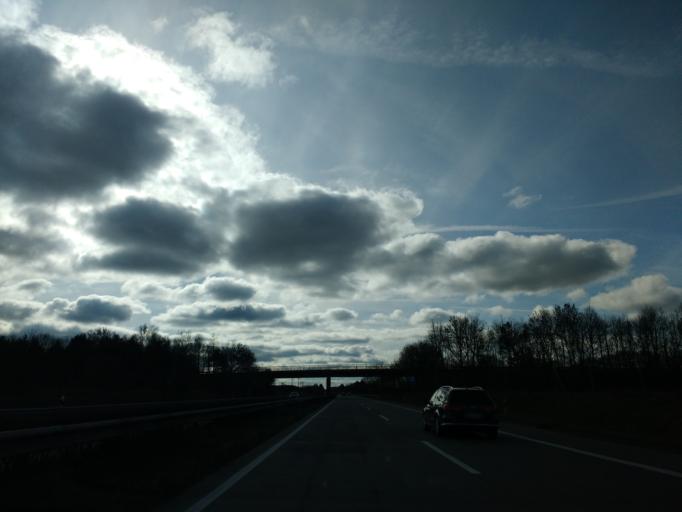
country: DE
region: Lower Saxony
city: Midlum
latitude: 53.6690
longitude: 8.6580
